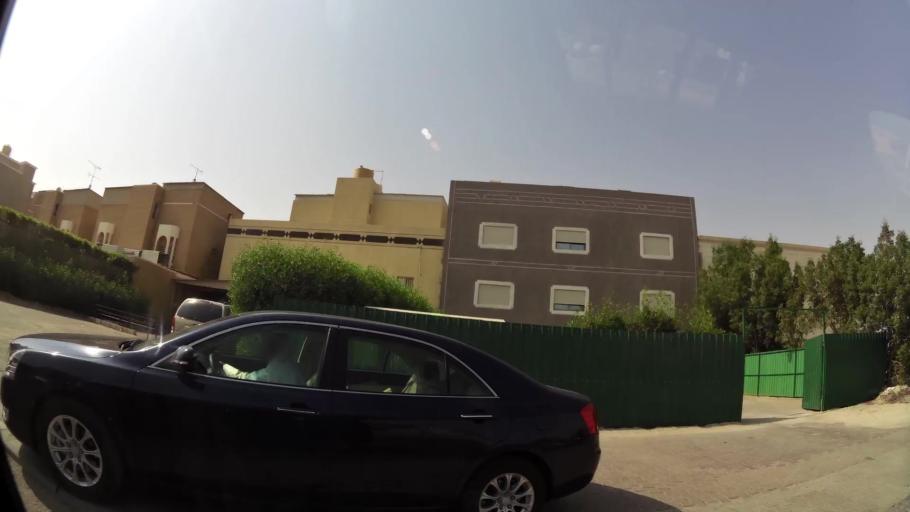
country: KW
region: Muhafazat al Jahra'
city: Al Jahra'
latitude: 29.3230
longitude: 47.6797
